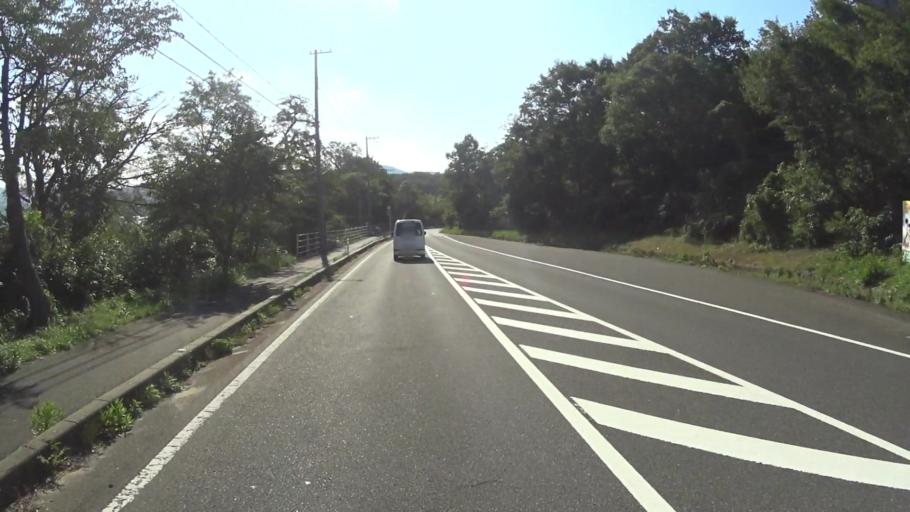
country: JP
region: Kyoto
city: Miyazu
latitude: 35.6958
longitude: 135.0505
